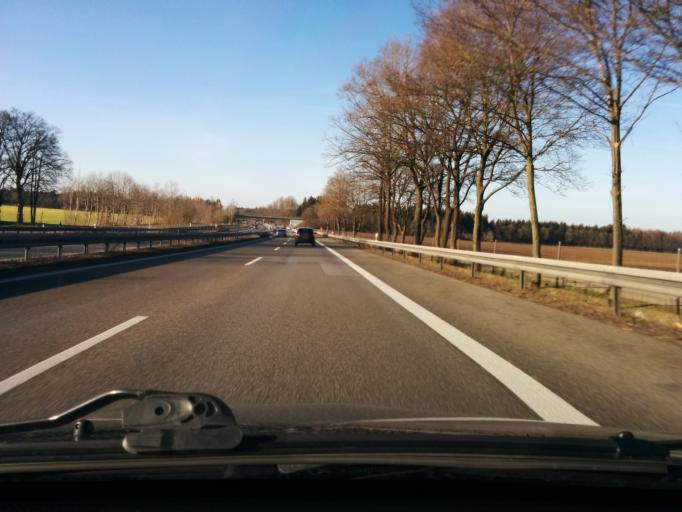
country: DE
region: Bavaria
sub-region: Upper Bavaria
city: Schwifting
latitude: 48.0582
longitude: 10.9596
